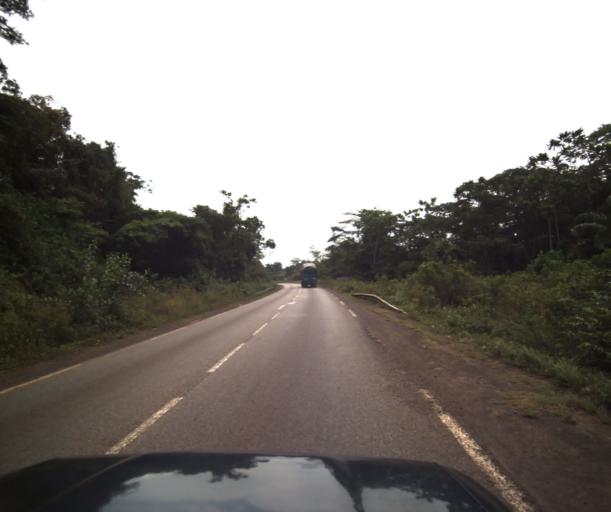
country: CM
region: Littoral
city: Edea
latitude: 3.8233
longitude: 10.3829
